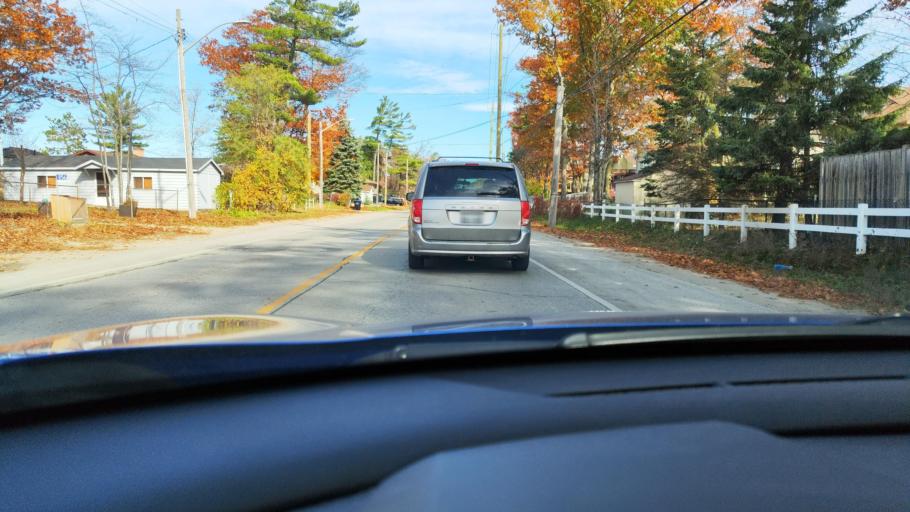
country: CA
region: Ontario
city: Wasaga Beach
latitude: 44.5164
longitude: -80.0212
